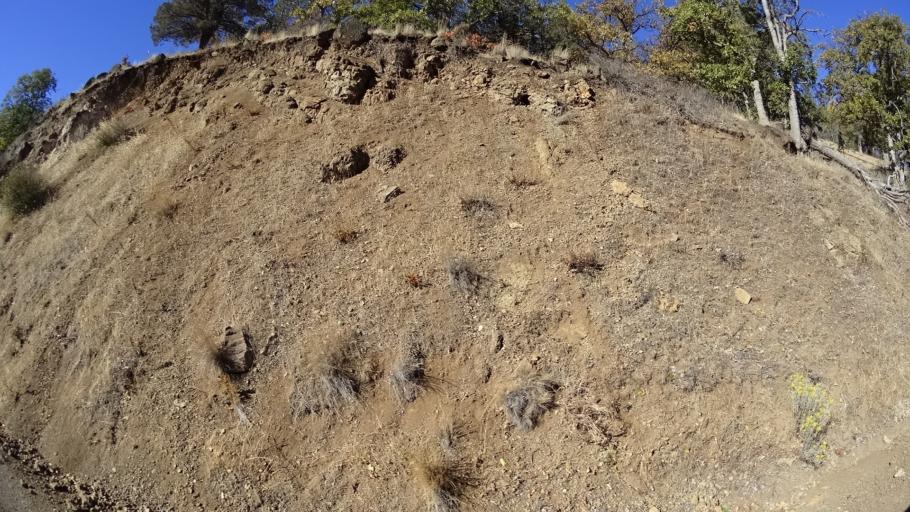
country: US
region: California
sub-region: Siskiyou County
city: Montague
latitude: 41.9338
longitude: -122.3545
